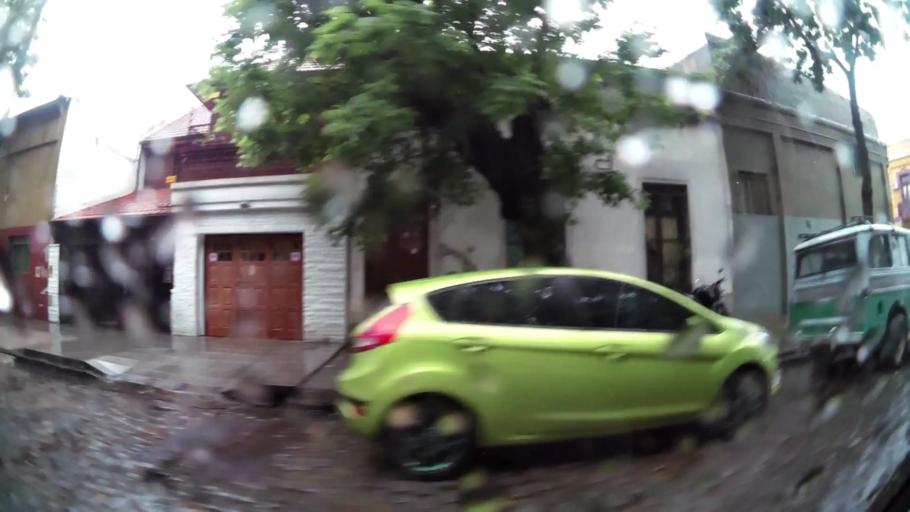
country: AR
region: Buenos Aires
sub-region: Partido de Avellaneda
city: Avellaneda
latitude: -34.6474
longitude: -58.3705
